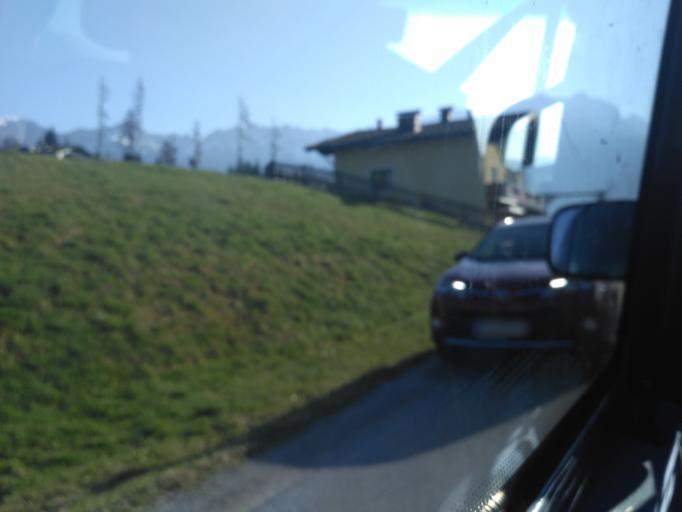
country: AT
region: Salzburg
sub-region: Politischer Bezirk Zell am See
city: Leogang
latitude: 47.4456
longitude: 12.7988
